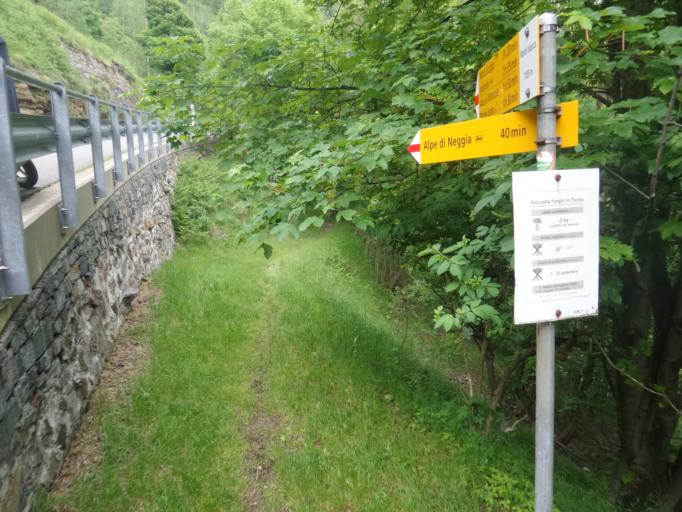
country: CH
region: Ticino
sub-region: Locarno District
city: Magadino
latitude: 46.1029
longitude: 8.8441
